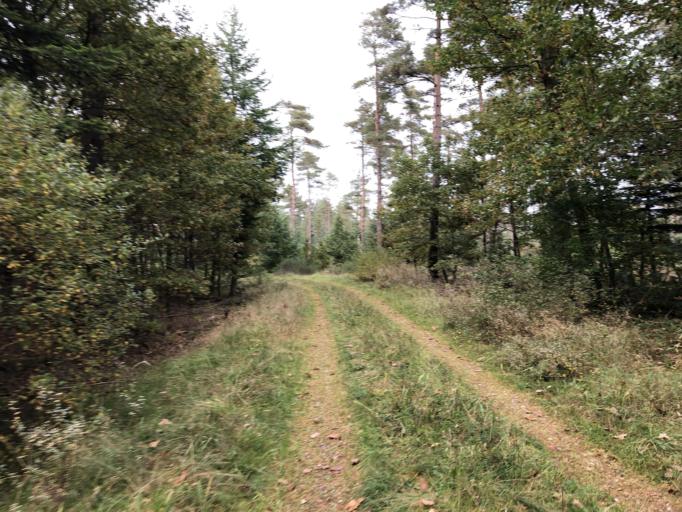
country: DK
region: Central Jutland
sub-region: Holstebro Kommune
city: Ulfborg
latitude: 56.2141
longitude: 8.4383
